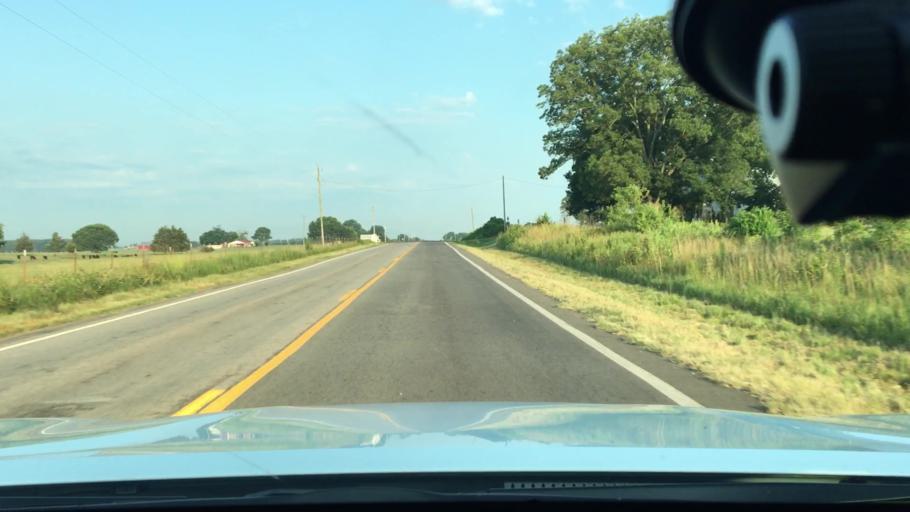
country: US
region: Arkansas
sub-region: Johnson County
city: Clarksville
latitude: 35.3787
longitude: -93.5353
